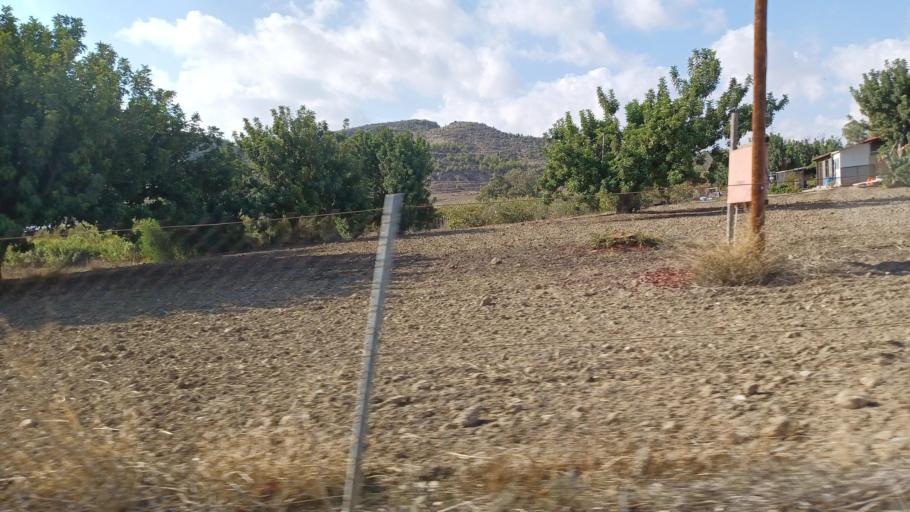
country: CY
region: Larnaka
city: Voroklini
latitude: 35.0018
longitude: 33.6529
